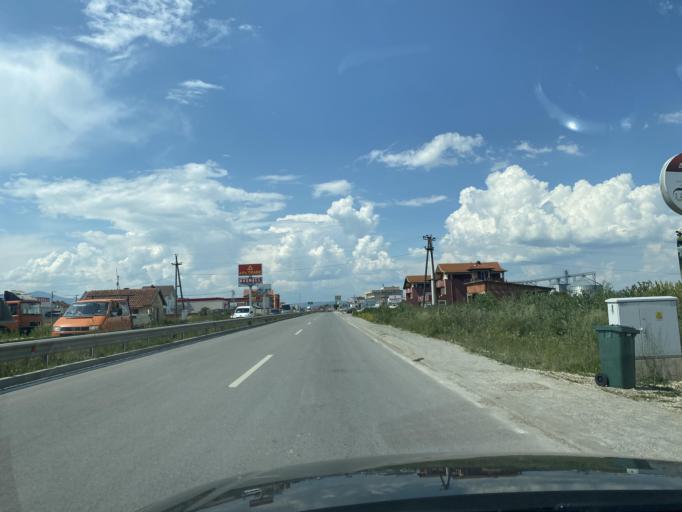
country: XK
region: Pristina
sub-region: Podujevo
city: Podujeva
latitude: 42.8766
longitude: 21.1818
